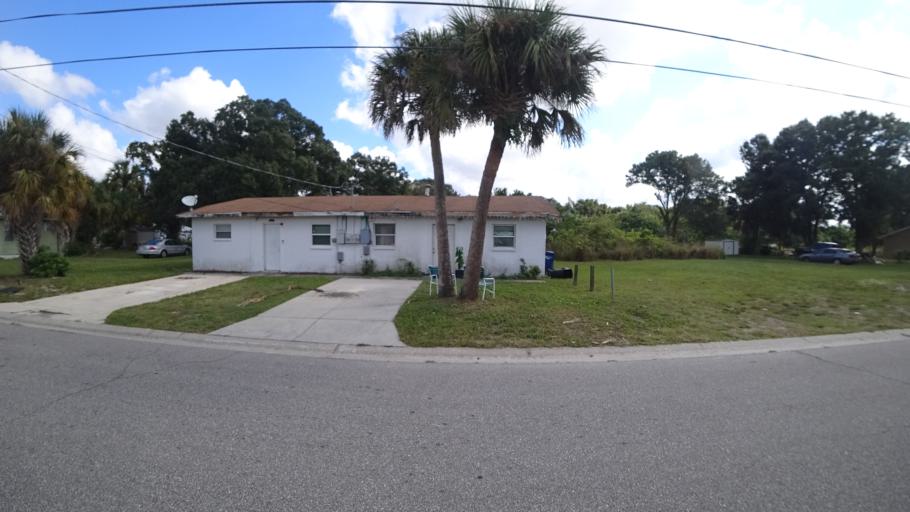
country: US
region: Florida
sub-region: Manatee County
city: Whitfield
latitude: 27.4022
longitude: -82.5431
